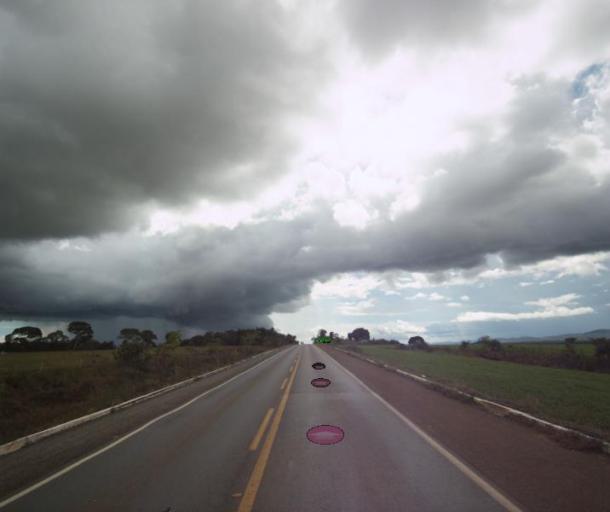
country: BR
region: Goias
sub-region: Uruacu
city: Uruacu
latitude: -14.6780
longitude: -49.1349
